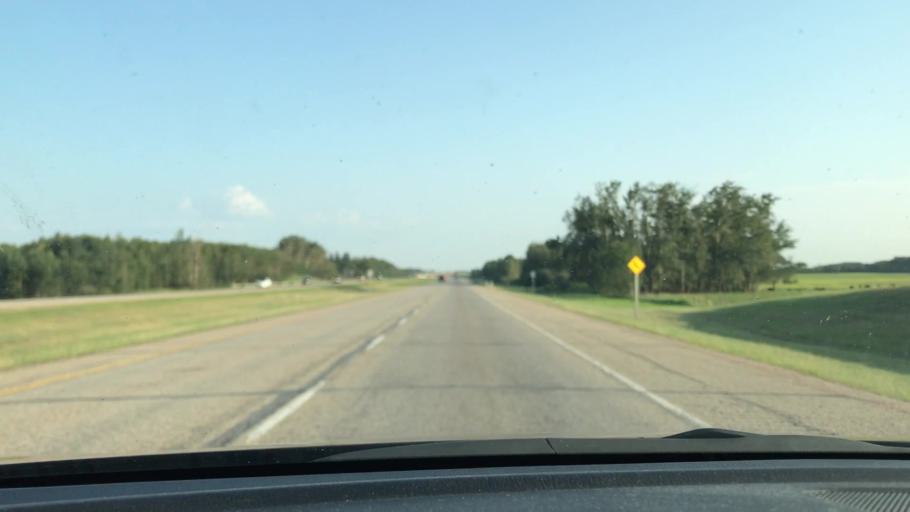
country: CA
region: Alberta
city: Lacombe
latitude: 52.5745
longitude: -113.6632
